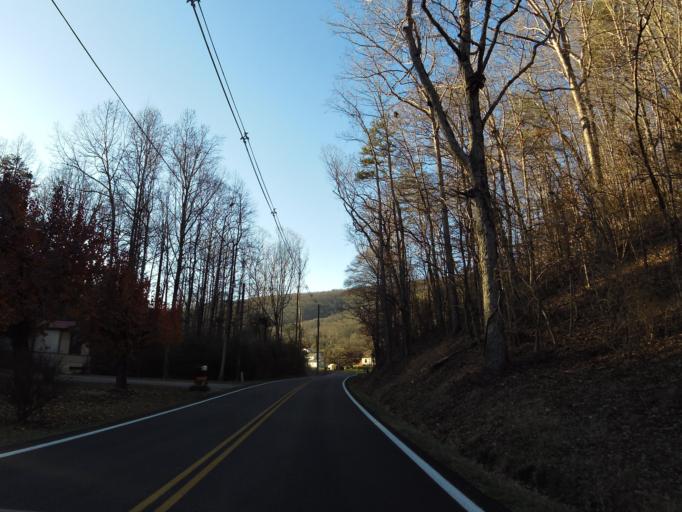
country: US
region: Tennessee
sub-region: Anderson County
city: Oak Ridge
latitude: 36.0762
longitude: -84.2521
